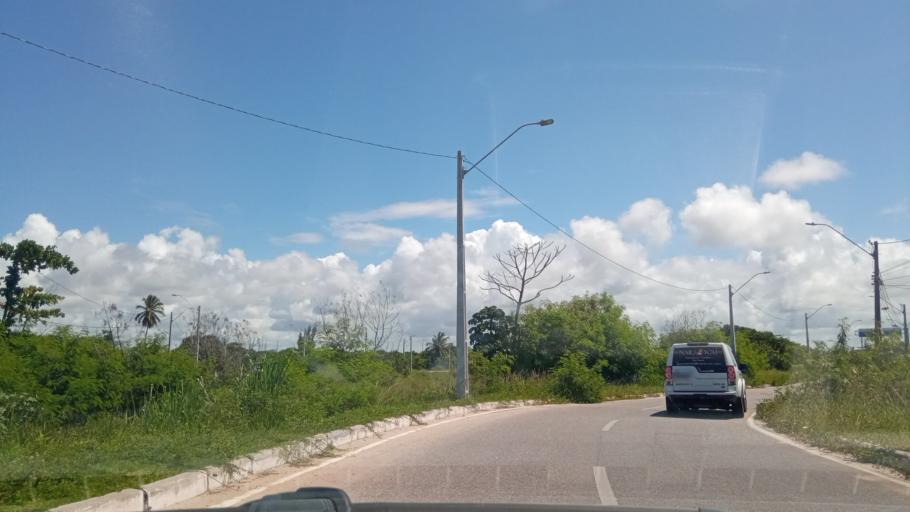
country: BR
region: Pernambuco
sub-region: Jaboatao Dos Guararapes
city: Jaboatao
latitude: -8.2379
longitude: -34.9377
